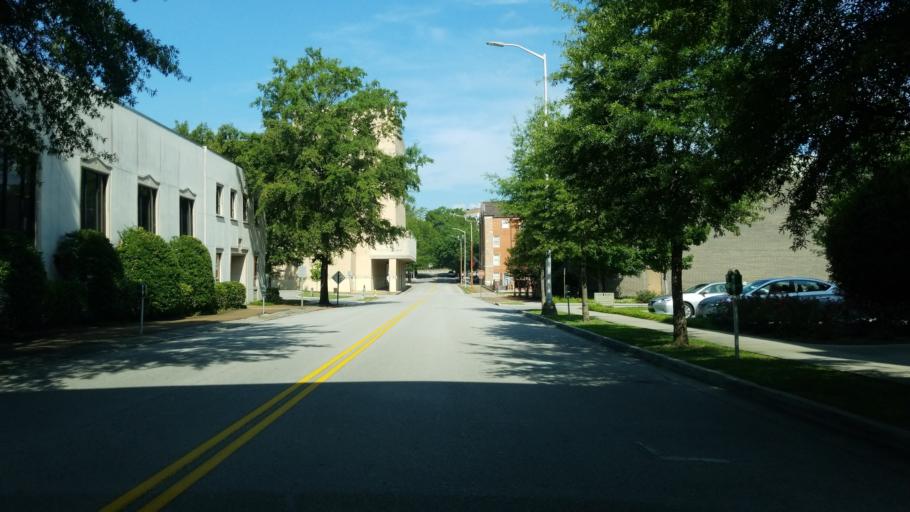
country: US
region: Tennessee
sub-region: Hamilton County
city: Chattanooga
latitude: 35.0480
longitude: -85.3041
